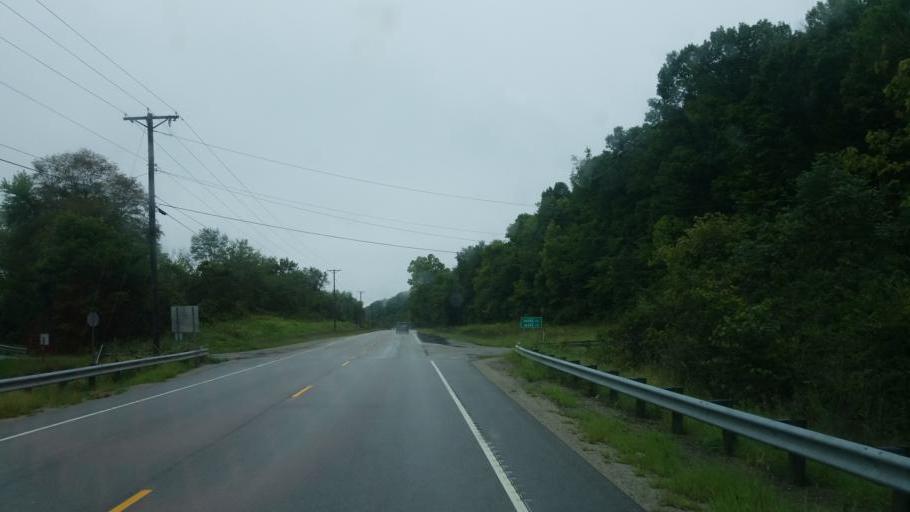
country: US
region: Kentucky
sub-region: Mason County
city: Maysville
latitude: 38.6448
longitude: -83.7049
